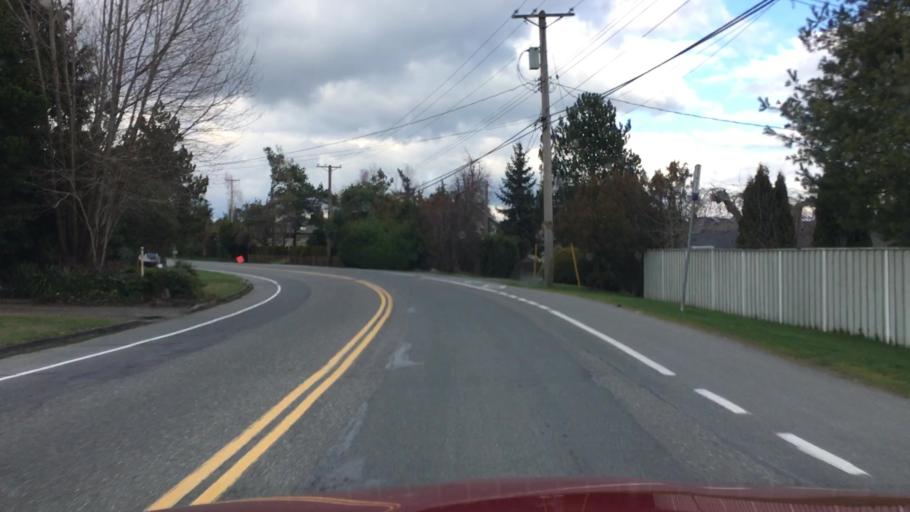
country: CA
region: British Columbia
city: North Saanich
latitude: 48.5990
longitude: -123.3946
